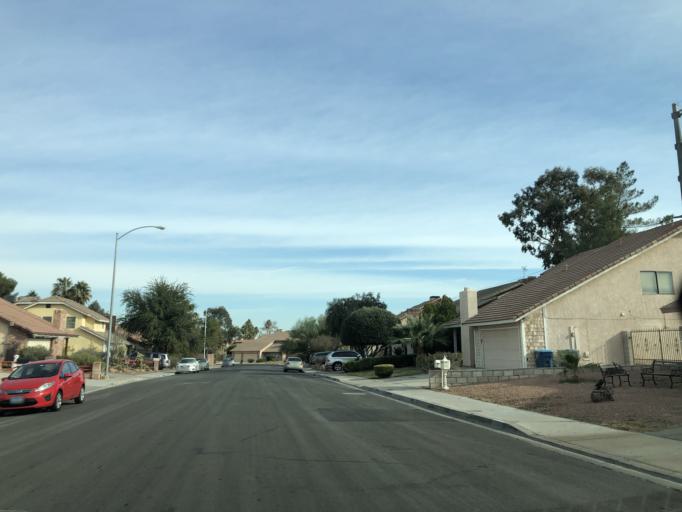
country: US
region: Nevada
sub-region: Clark County
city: Winchester
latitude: 36.1169
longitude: -115.1256
